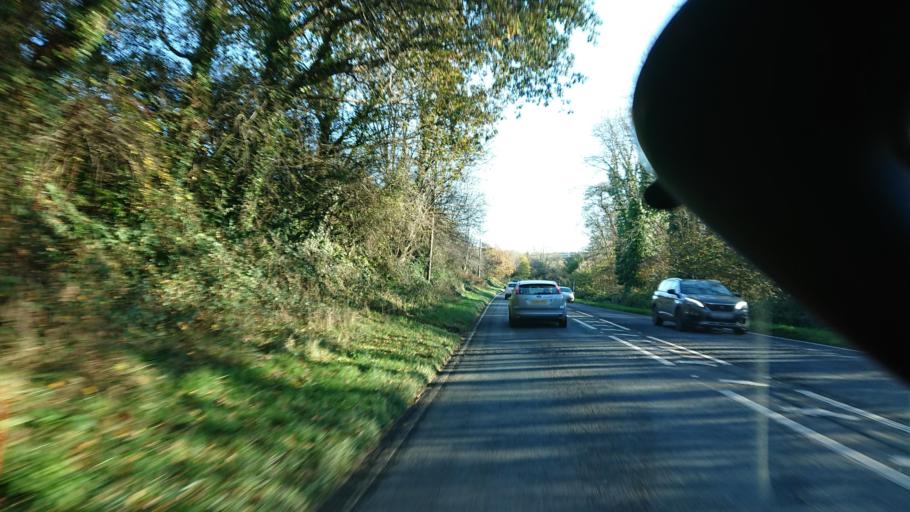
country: GB
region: England
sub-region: Cornwall
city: Pillaton
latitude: 50.3946
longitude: -4.3464
